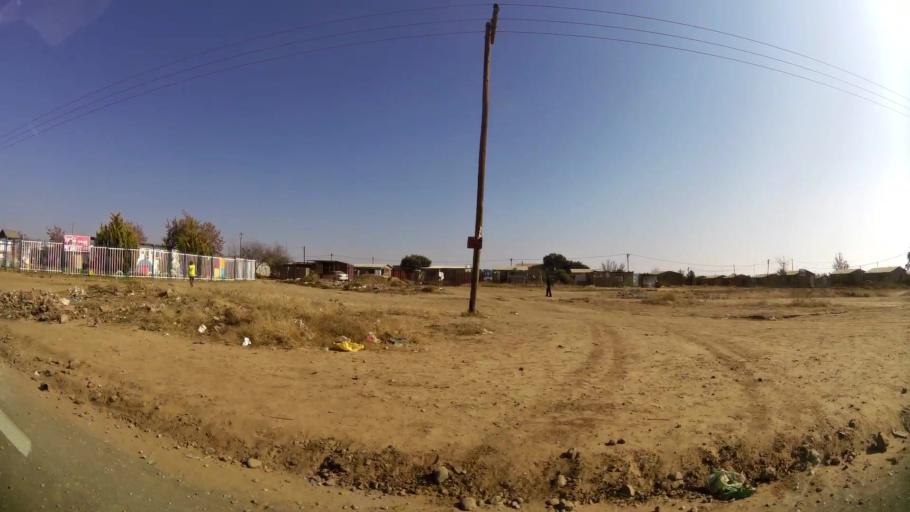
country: ZA
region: Orange Free State
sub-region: Mangaung Metropolitan Municipality
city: Bloemfontein
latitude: -29.1823
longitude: 26.2858
